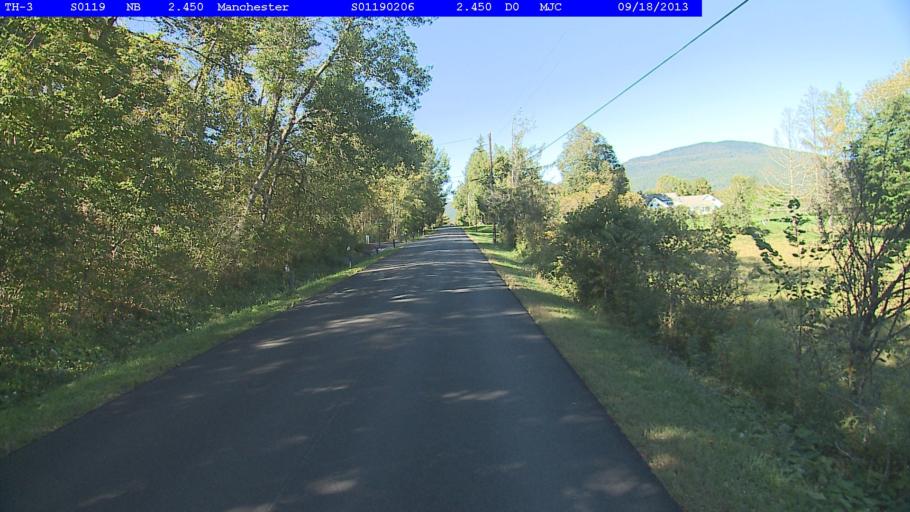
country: US
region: Vermont
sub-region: Bennington County
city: Manchester Center
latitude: 43.1984
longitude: -73.0695
